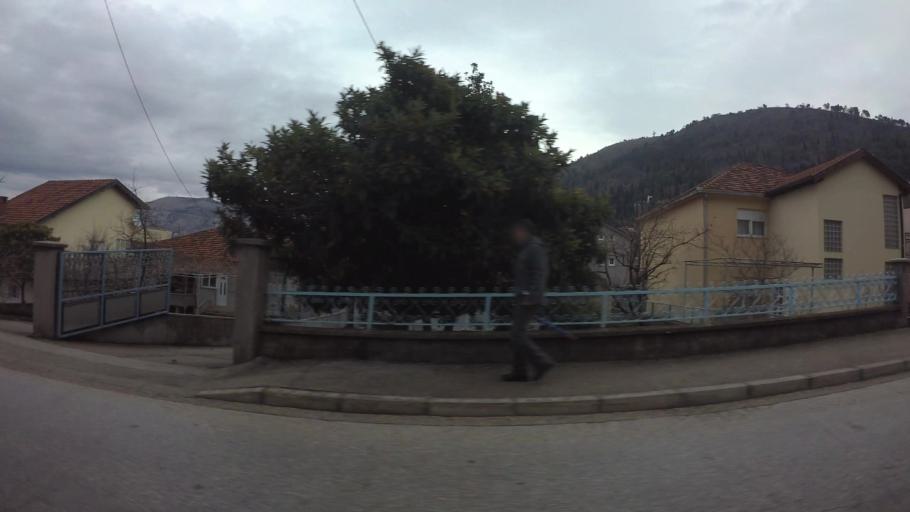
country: BA
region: Federation of Bosnia and Herzegovina
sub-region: Hercegovacko-Bosanski Kanton
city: Mostar
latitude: 43.3338
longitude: 17.7960
